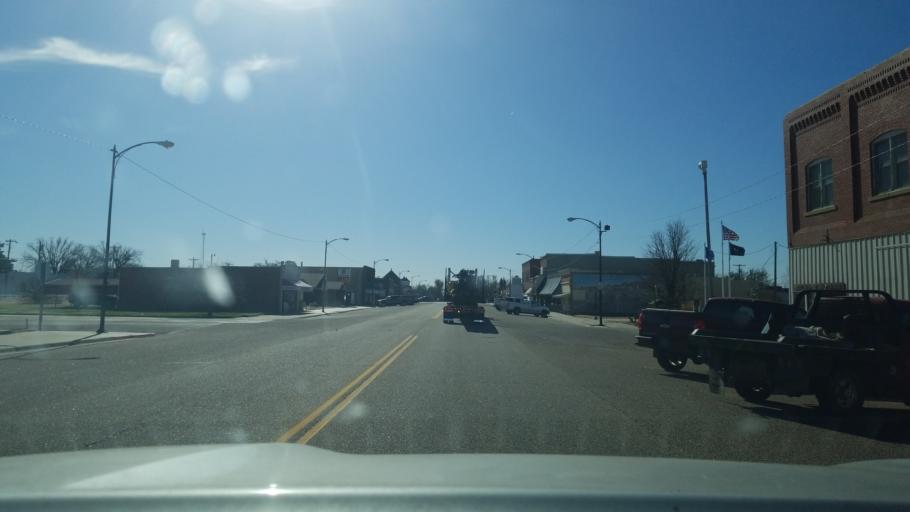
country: US
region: Kansas
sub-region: Kiowa County
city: Greensburg
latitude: 37.5509
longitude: -99.6341
